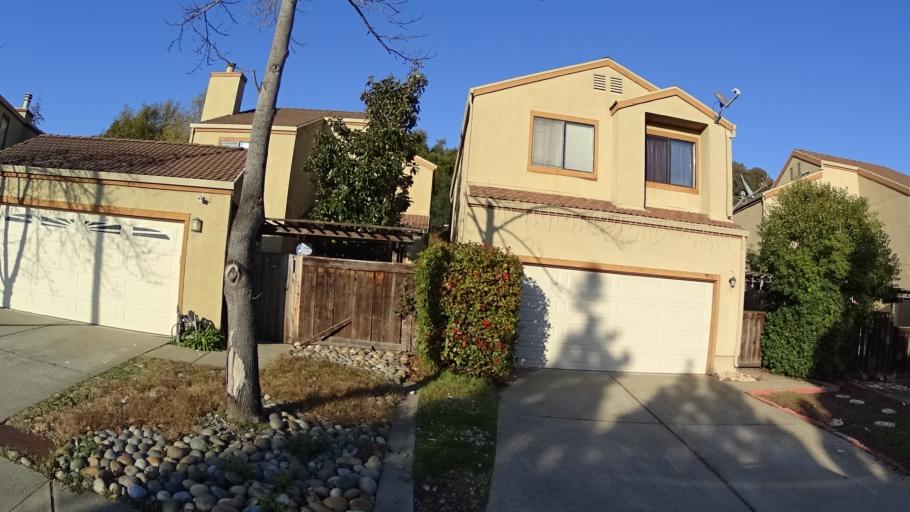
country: US
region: California
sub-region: Alameda County
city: Fairview
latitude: 37.6504
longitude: -122.0399
